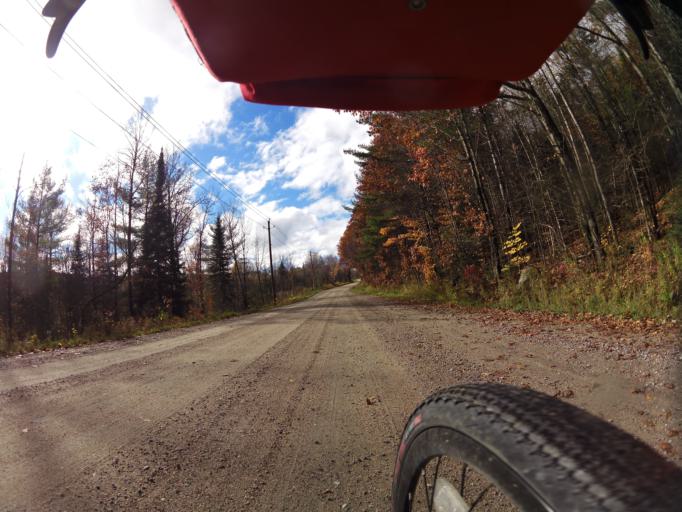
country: CA
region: Quebec
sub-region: Outaouais
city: Wakefield
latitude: 45.6971
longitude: -76.0499
